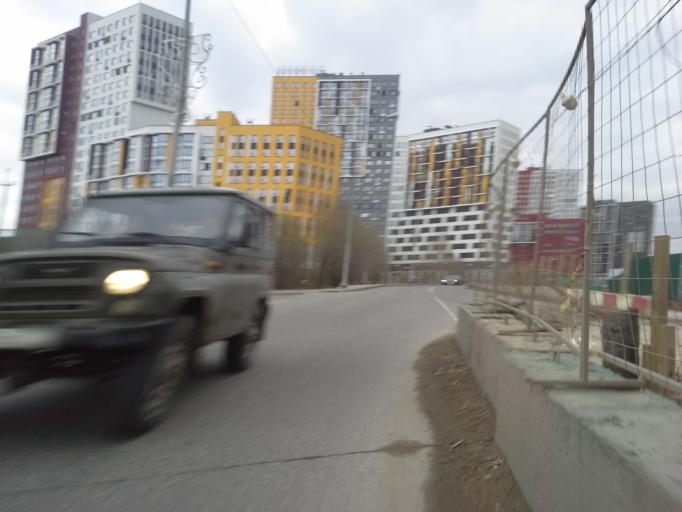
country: RU
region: Moskovskaya
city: Kommunarka
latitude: 55.5778
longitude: 37.4752
